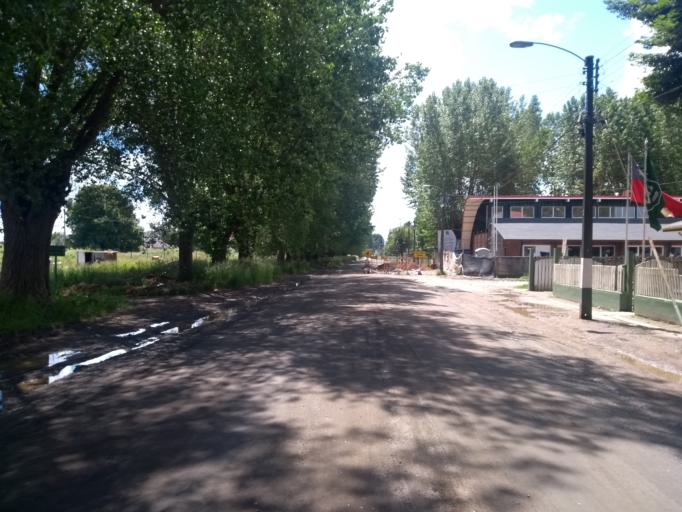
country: CL
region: Los Lagos
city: Las Animas
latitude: -39.6666
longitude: -72.9483
